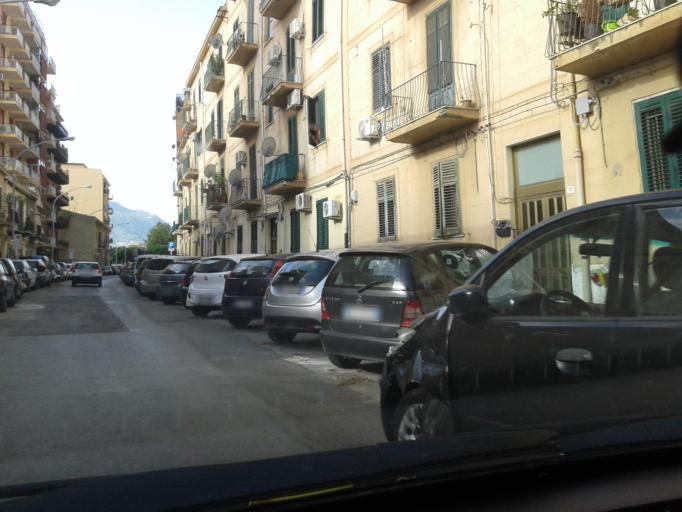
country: IT
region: Sicily
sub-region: Palermo
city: Palermo
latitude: 38.1000
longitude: 13.3385
